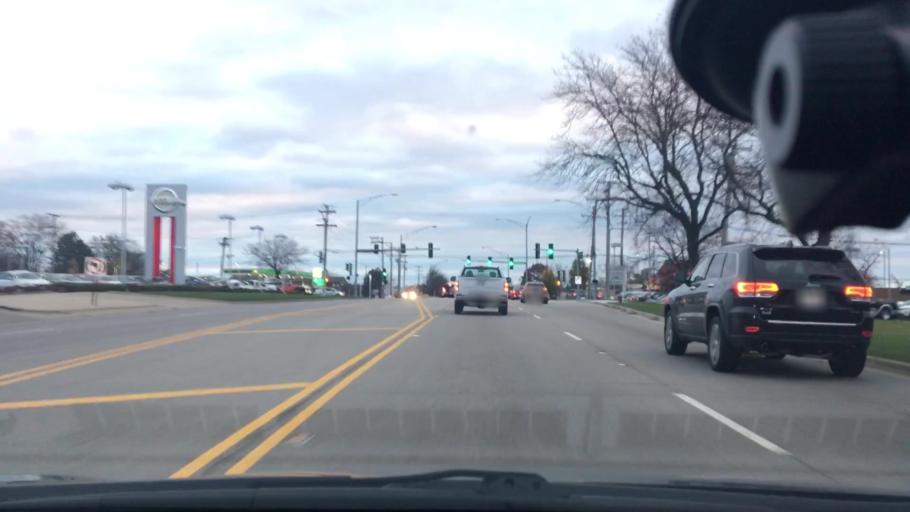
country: US
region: Illinois
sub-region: Lake County
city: Long Grove
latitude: 42.1391
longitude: -87.9975
